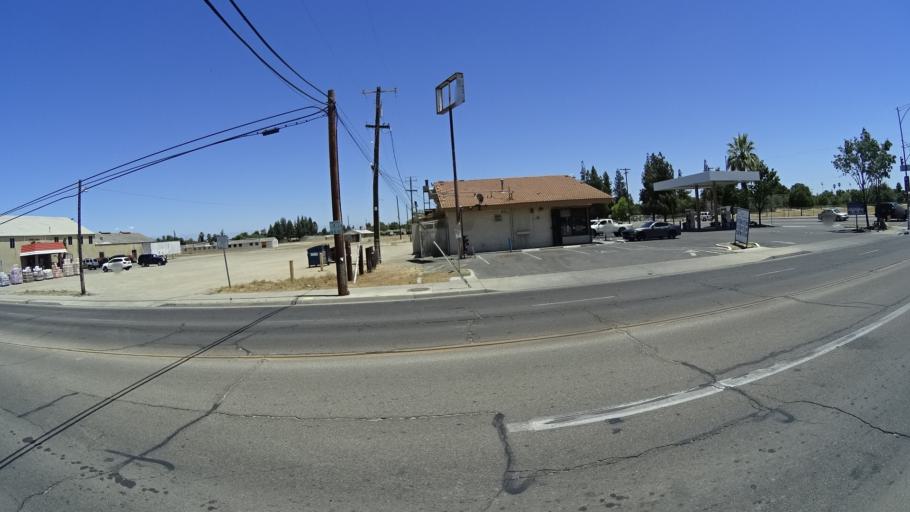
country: US
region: California
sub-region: Fresno County
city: Fresno
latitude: 36.7290
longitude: -119.7456
